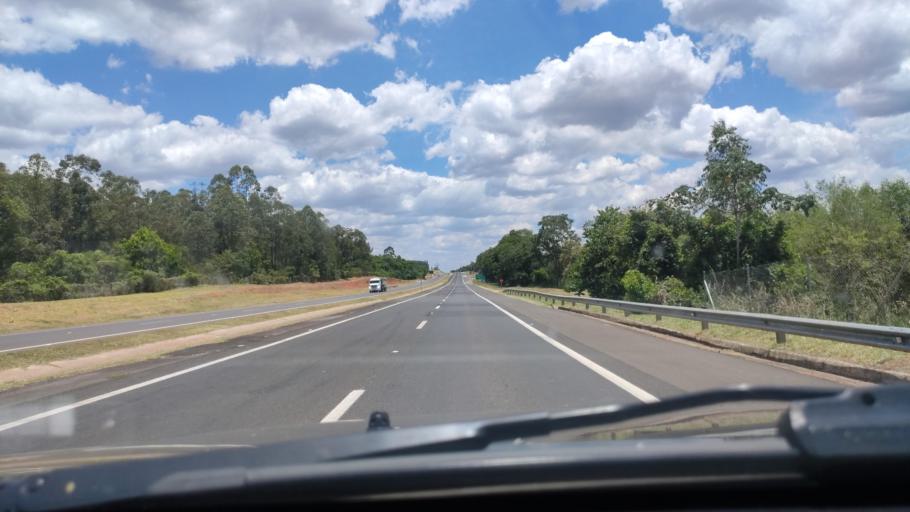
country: BR
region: Sao Paulo
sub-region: Duartina
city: Duartina
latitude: -22.5091
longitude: -49.2969
